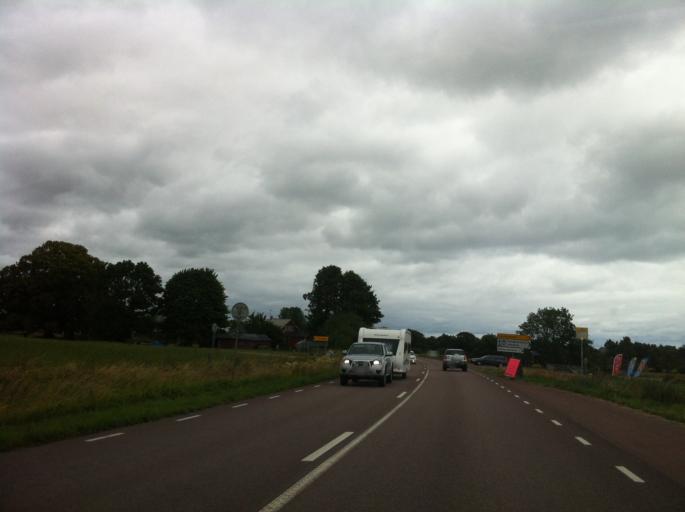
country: SE
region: Kalmar
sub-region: Borgholms Kommun
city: Borgholm
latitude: 57.1725
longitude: 17.0249
